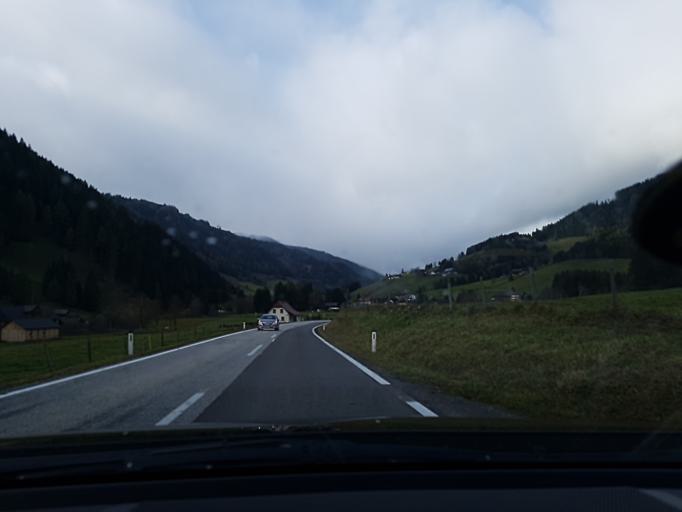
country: AT
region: Styria
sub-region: Politischer Bezirk Murtal
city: Sankt Johann am Tauern
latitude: 47.3133
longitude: 14.4828
